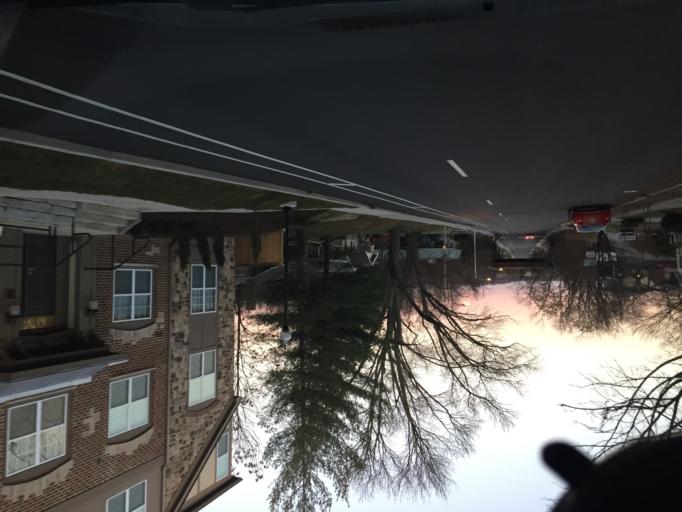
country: US
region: Indiana
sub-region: Monroe County
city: Bloomington
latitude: 39.1736
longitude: -86.5336
